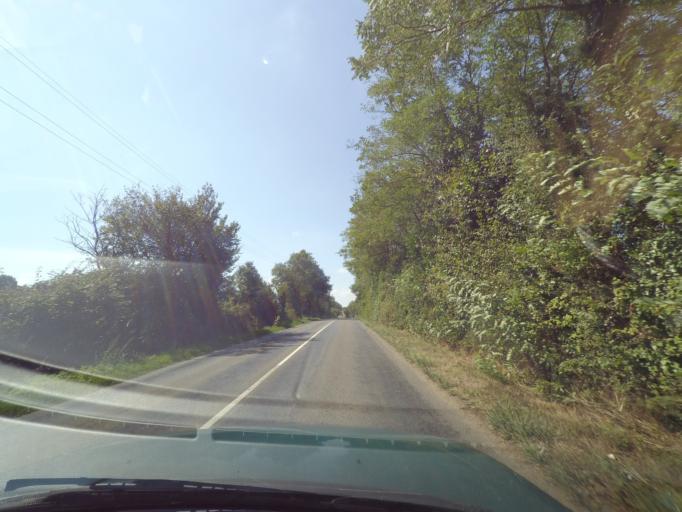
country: FR
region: Pays de la Loire
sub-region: Departement de la Loire-Atlantique
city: Saint-Philbert-de-Grand-Lieu
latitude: 47.0347
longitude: -1.6632
